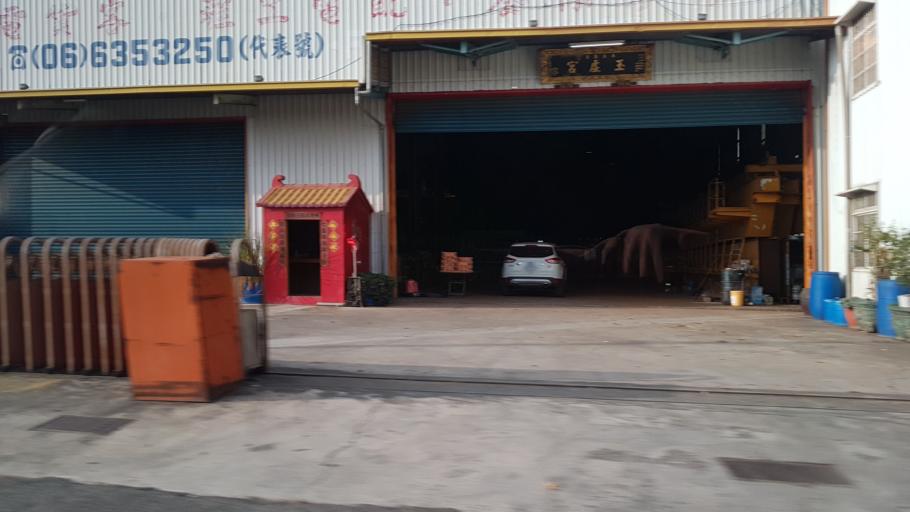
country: TW
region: Taiwan
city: Xinying
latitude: 23.3440
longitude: 120.3524
